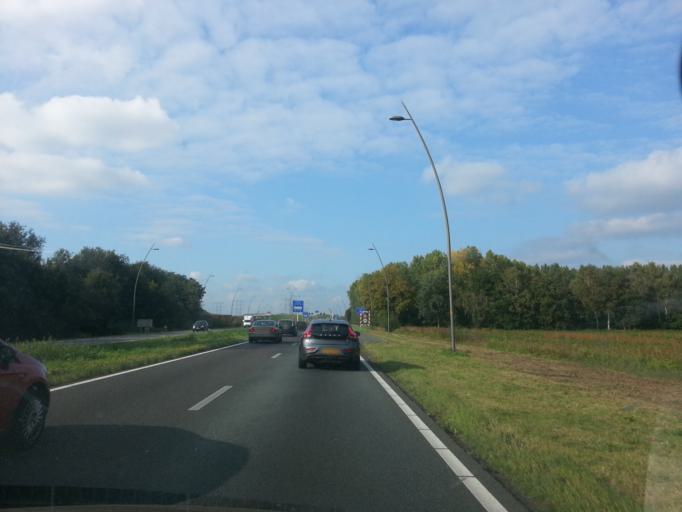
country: NL
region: North Brabant
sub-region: Gemeente Son en Breugel
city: Son
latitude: 51.4928
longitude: 5.4836
